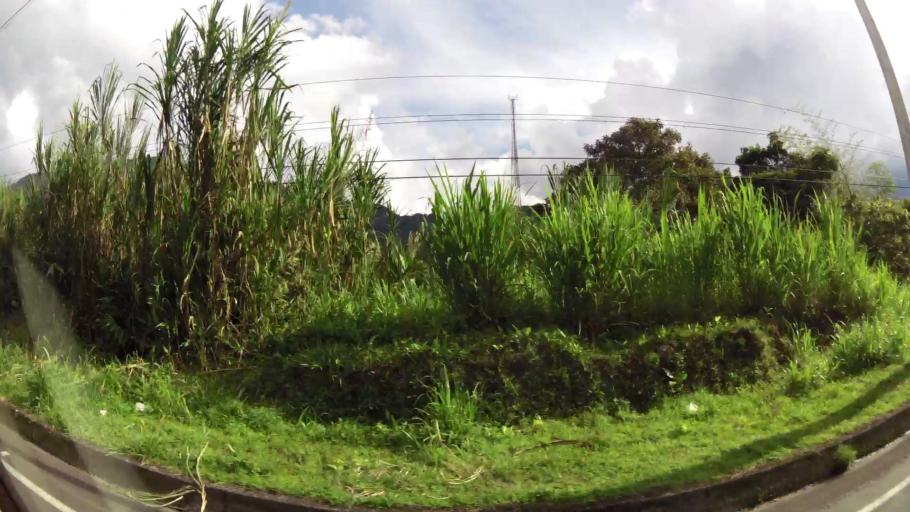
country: EC
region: Pastaza
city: Puyo
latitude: -1.4126
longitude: -78.2064
